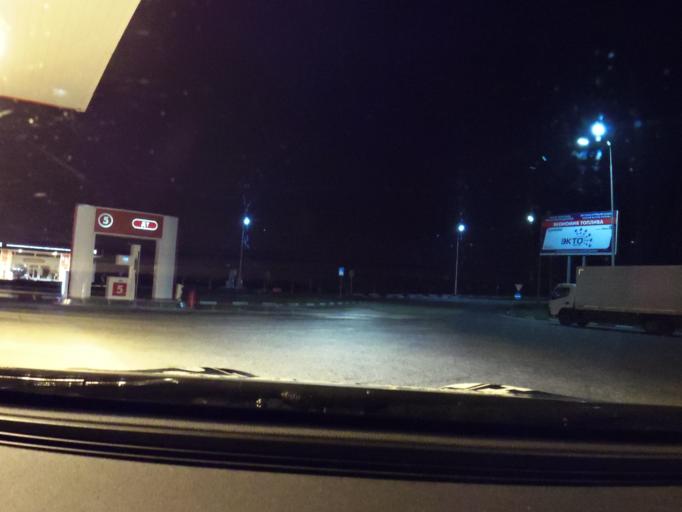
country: RU
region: Chelyabinsk
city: Kropachevo
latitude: 54.9712
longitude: 57.9255
